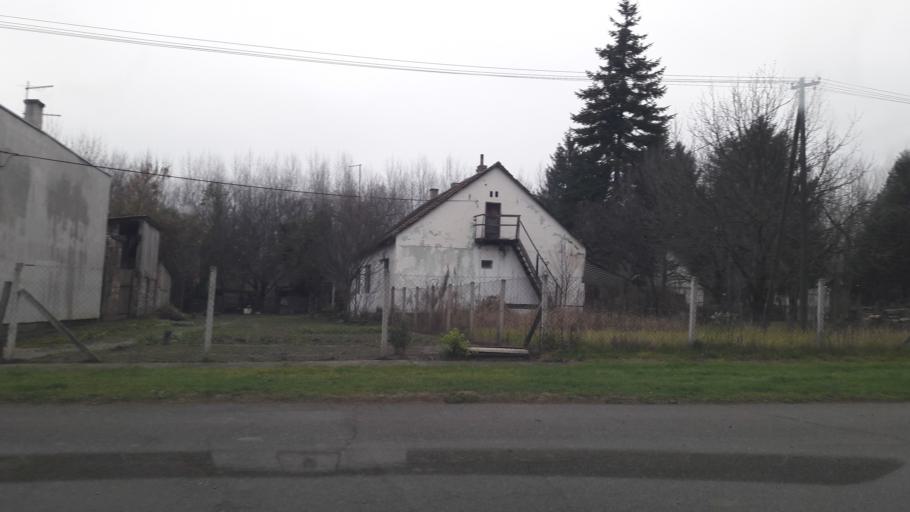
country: HR
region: Osjecko-Baranjska
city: Visnjevac
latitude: 45.5720
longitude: 18.6137
